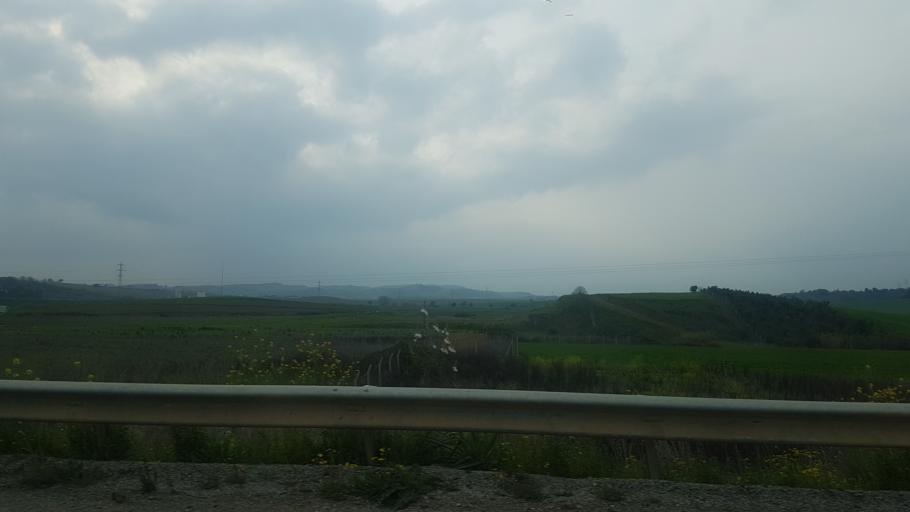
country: TR
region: Mersin
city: Yenice
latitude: 37.0644
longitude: 35.1709
